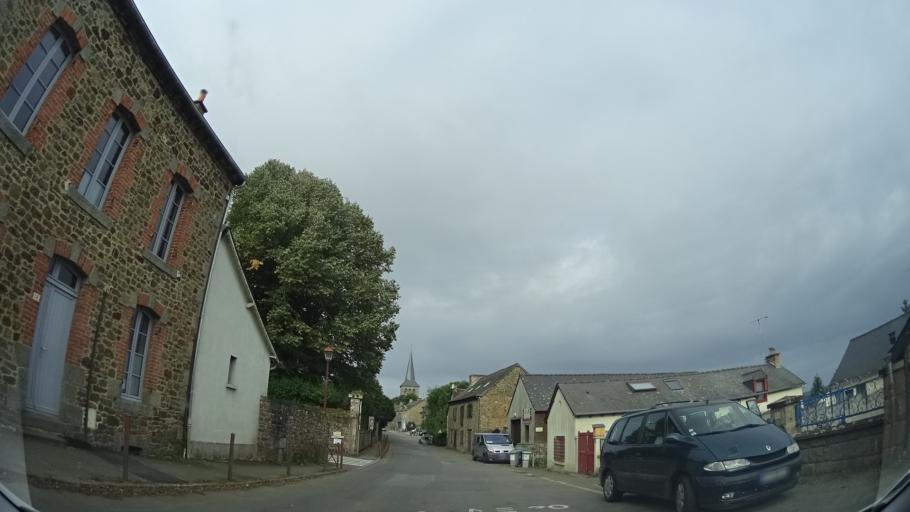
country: FR
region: Brittany
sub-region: Departement d'Ille-et-Vilaine
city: Hede-Bazouges
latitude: 48.2970
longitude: -1.7979
